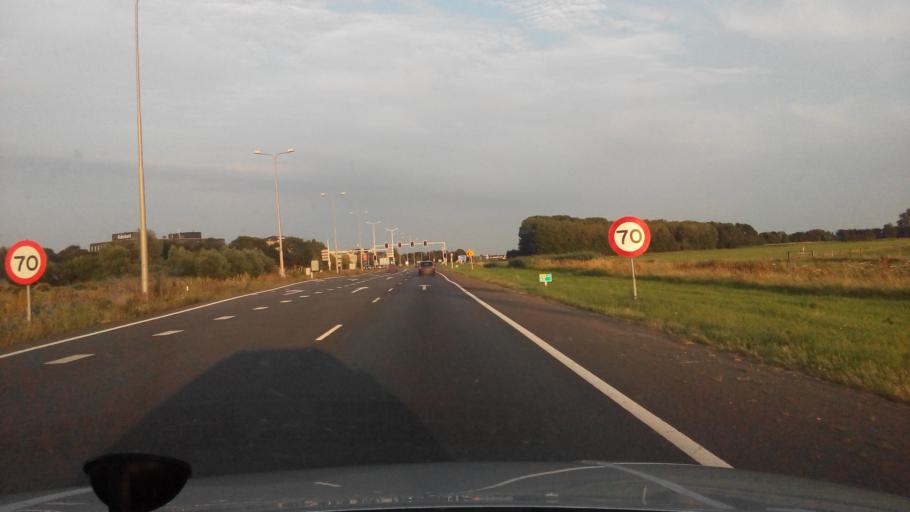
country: NL
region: South Holland
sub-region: Gemeente Alphen aan den Rijn
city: Alphen aan den Rijn
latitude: 52.1245
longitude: 4.6228
